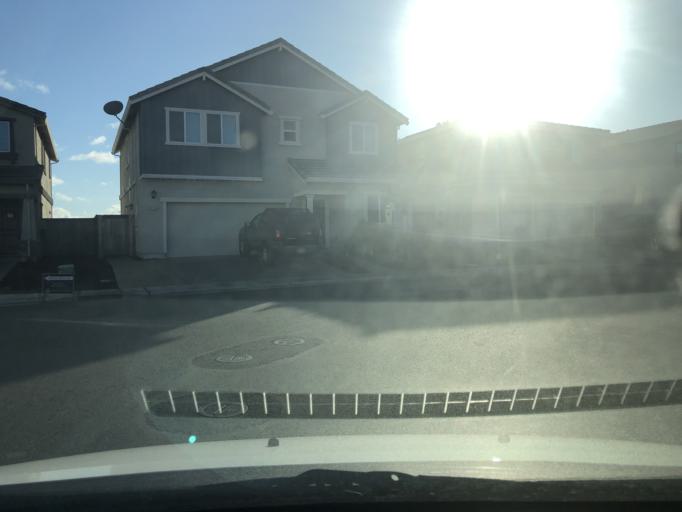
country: US
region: California
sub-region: Sacramento County
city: Antelope
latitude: 38.7698
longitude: -121.3817
